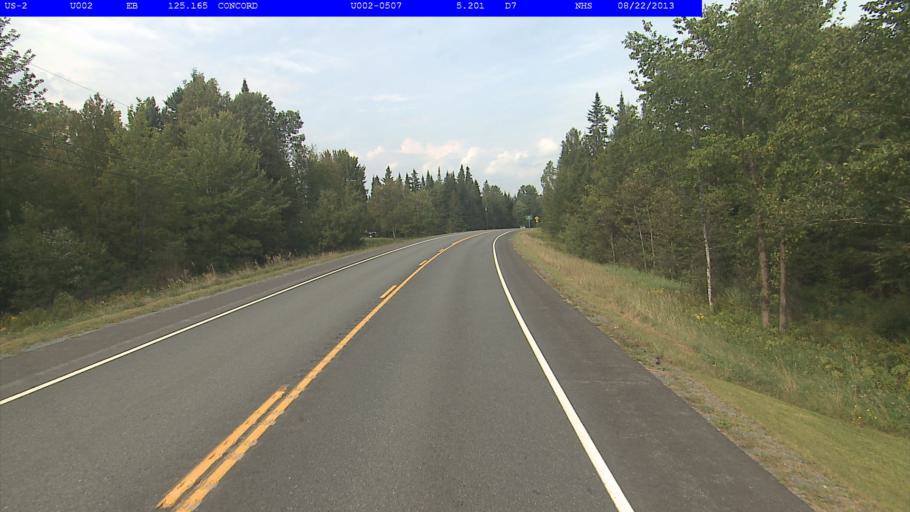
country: US
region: Vermont
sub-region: Caledonia County
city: Lyndonville
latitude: 44.4660
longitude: -71.8601
